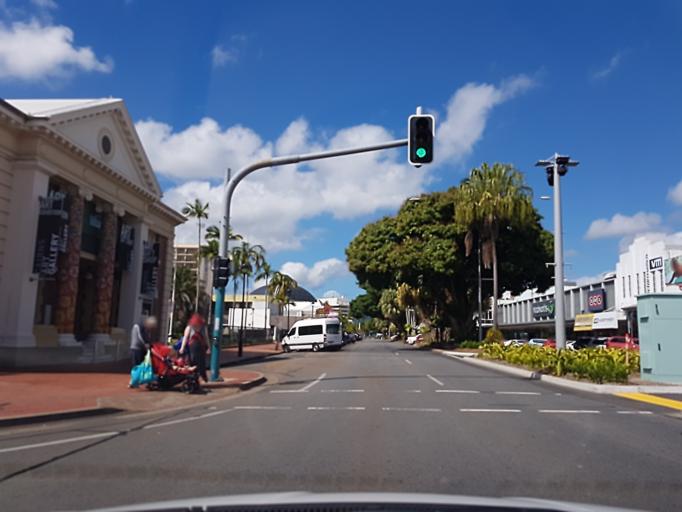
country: AU
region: Queensland
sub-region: Cairns
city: Cairns
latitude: -16.9213
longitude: 145.7769
